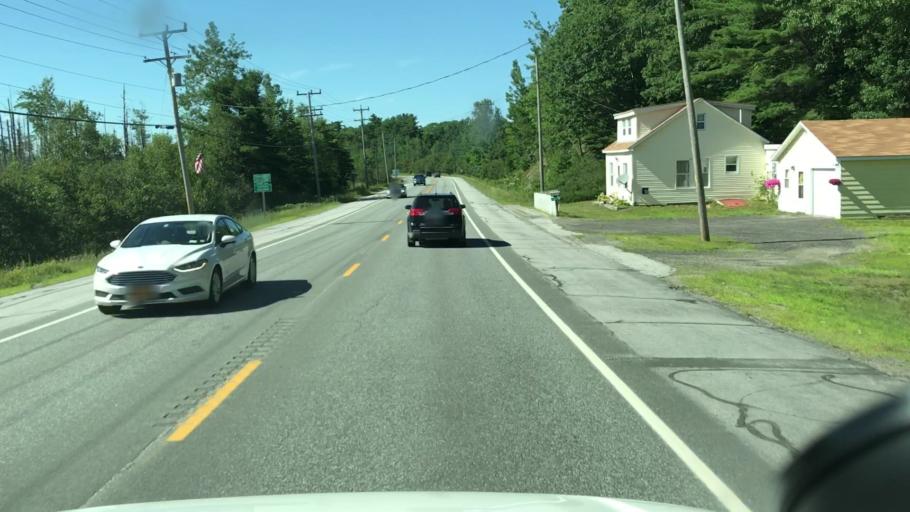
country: US
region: Maine
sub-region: Hancock County
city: Dedham
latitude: 44.7310
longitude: -68.6242
